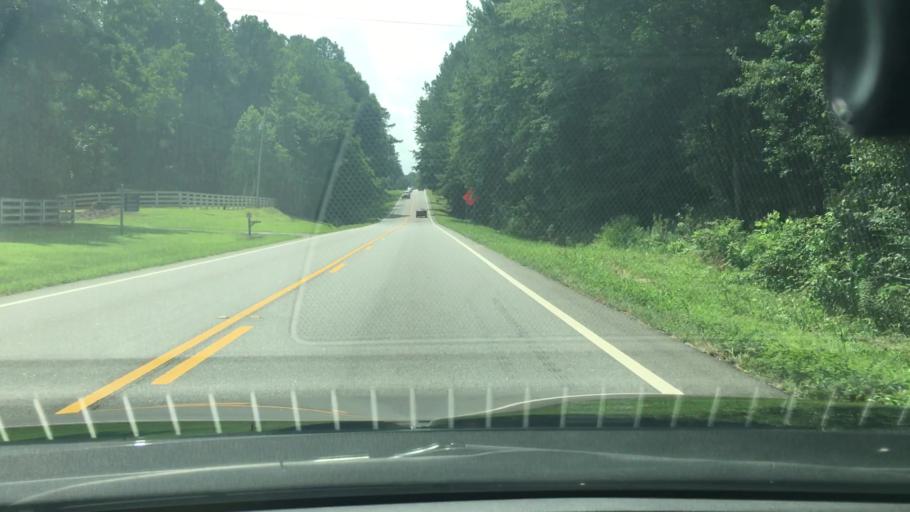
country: US
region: Georgia
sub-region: Coweta County
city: East Newnan
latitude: 33.3339
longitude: -84.7140
